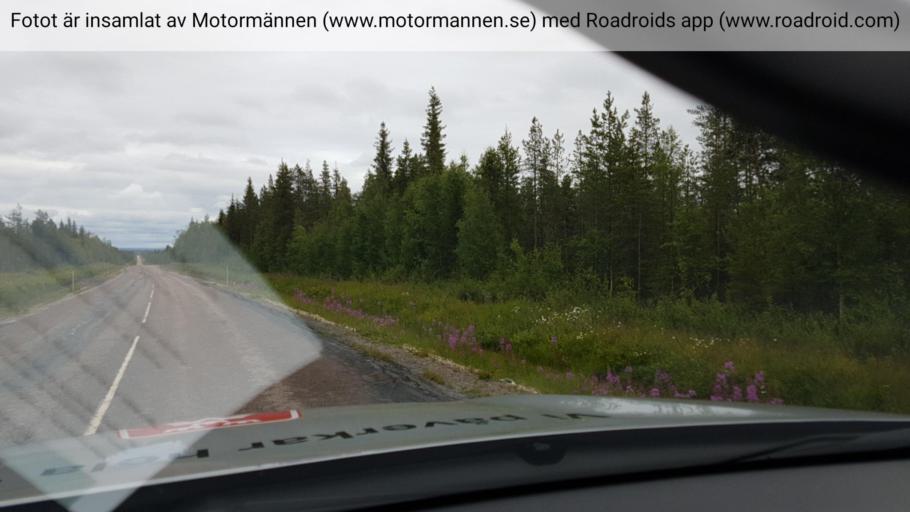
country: SE
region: Norrbotten
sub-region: Overkalix Kommun
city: OEverkalix
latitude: 67.0660
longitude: 22.4112
